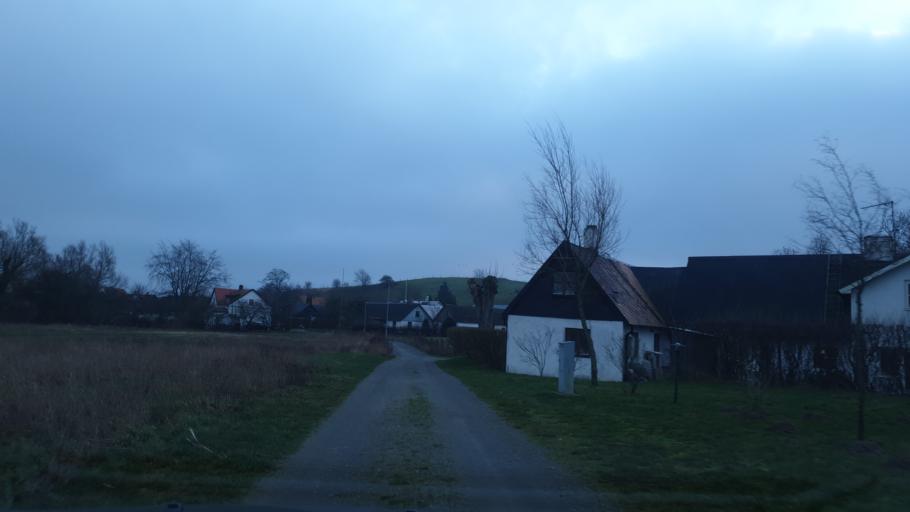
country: SE
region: Skane
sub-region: Ystads Kommun
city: Kopingebro
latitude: 55.3867
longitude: 14.0610
